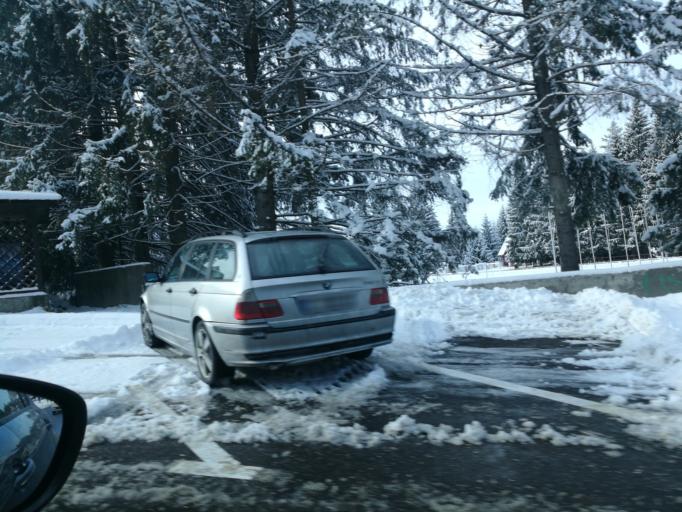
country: RO
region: Brasov
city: Brasov
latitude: 45.5893
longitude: 25.5512
